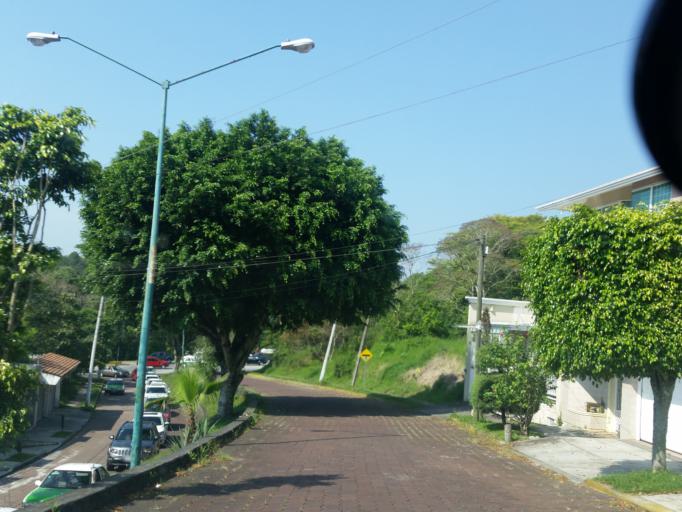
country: MX
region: Veracruz
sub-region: Xalapa
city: Xalapa de Enriquez
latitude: 19.5200
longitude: -96.9031
